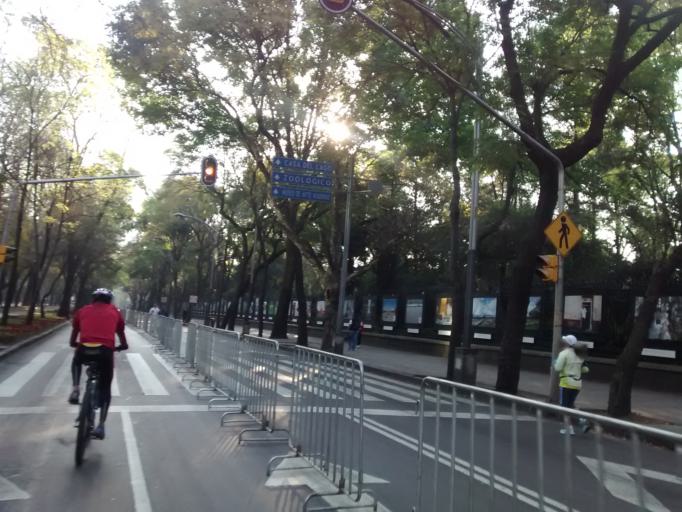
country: MX
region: Mexico City
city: Polanco
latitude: 19.4254
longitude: -99.1902
